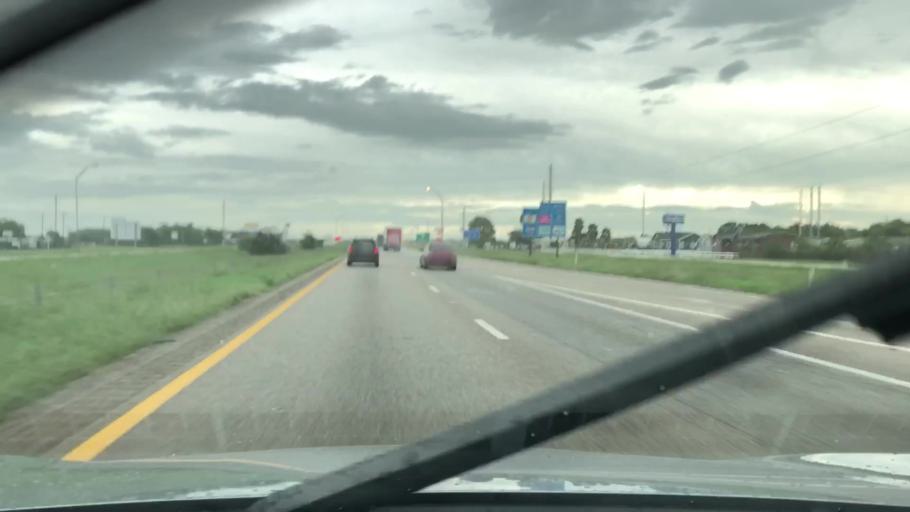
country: US
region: Texas
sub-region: Guadalupe County
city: Seguin
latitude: 29.5992
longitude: -97.9605
